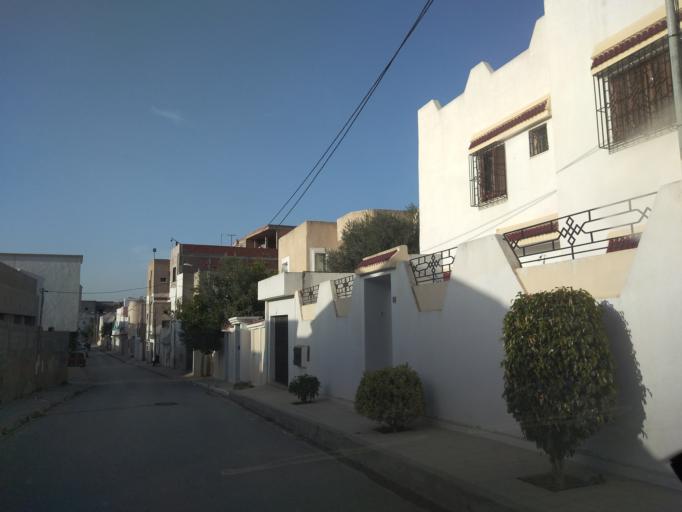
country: TN
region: Manouba
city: Manouba
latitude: 36.7976
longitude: 10.0901
